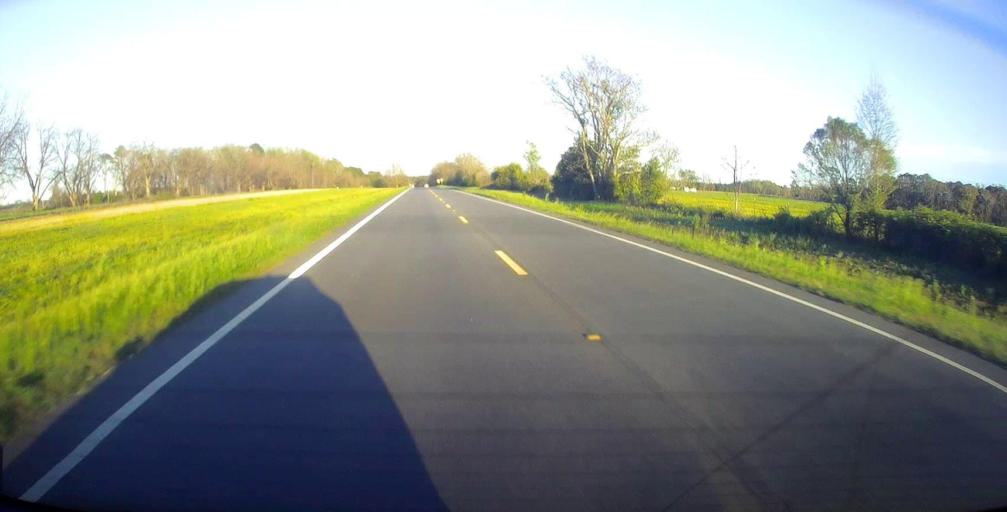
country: US
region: Georgia
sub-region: Wilcox County
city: Rochelle
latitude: 31.9455
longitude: -83.5285
